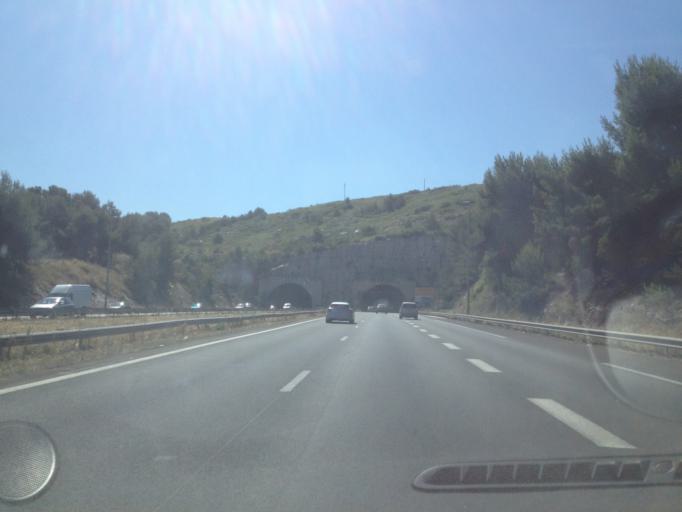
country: FR
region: Provence-Alpes-Cote d'Azur
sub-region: Departement des Bouches-du-Rhone
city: Les Pennes-Mirabeau
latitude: 43.4134
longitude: 5.2801
